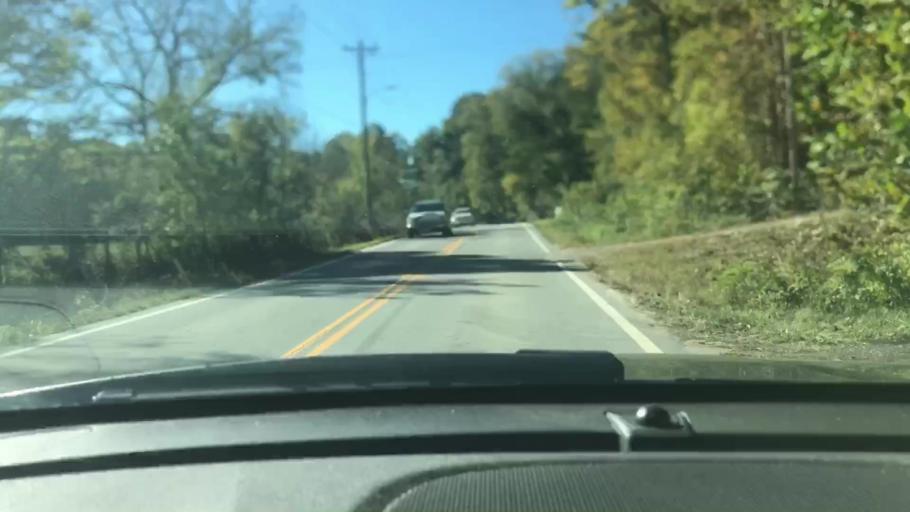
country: US
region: Tennessee
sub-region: Dickson County
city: Charlotte
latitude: 36.1816
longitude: -87.3183
